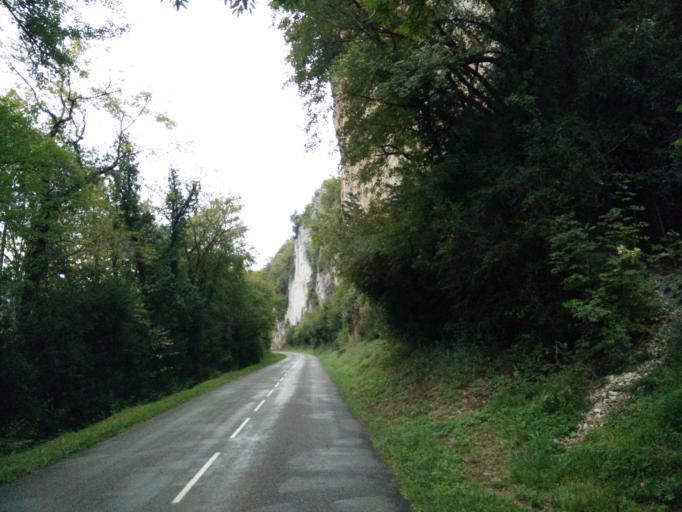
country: FR
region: Midi-Pyrenees
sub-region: Departement du Lot
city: Lalbenque
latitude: 44.4858
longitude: 1.6500
